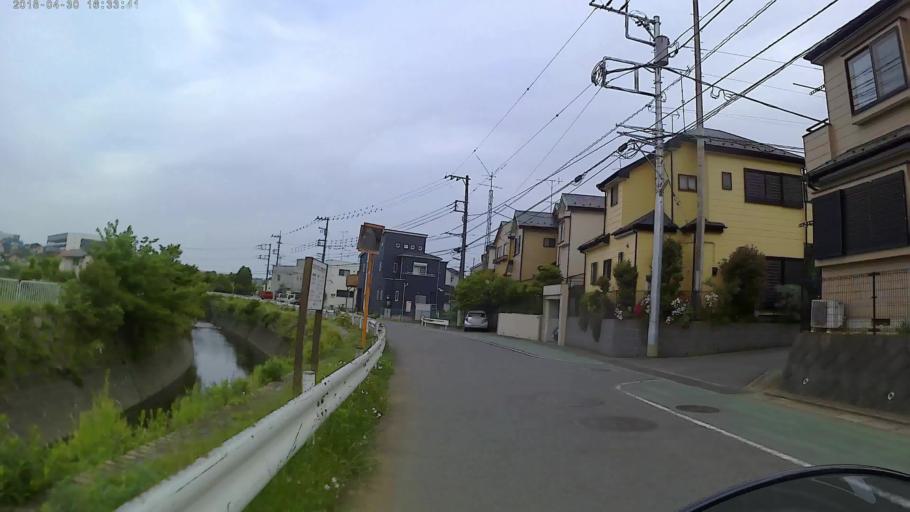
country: JP
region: Kanagawa
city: Zama
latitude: 35.4496
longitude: 139.4055
